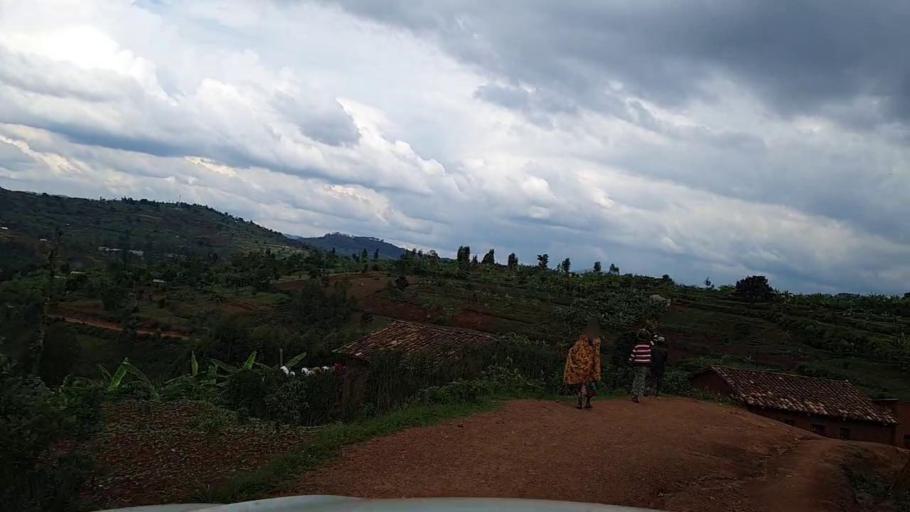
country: RW
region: Southern Province
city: Gikongoro
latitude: -2.4206
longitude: 29.6522
